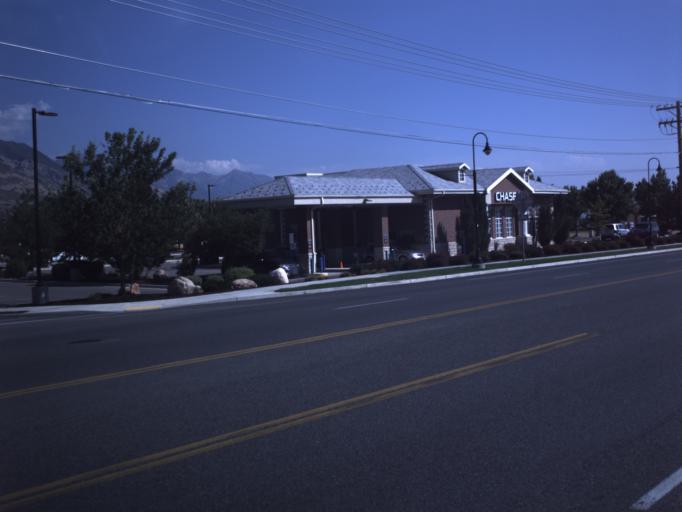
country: US
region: Utah
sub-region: Utah County
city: Cedar Hills
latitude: 40.4166
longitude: -111.7736
